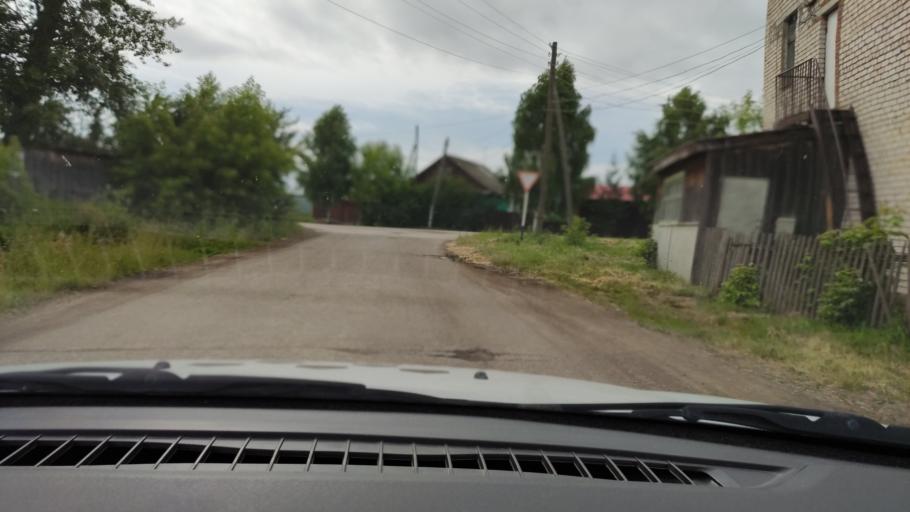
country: RU
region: Perm
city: Orda
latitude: 57.2987
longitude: 56.6567
